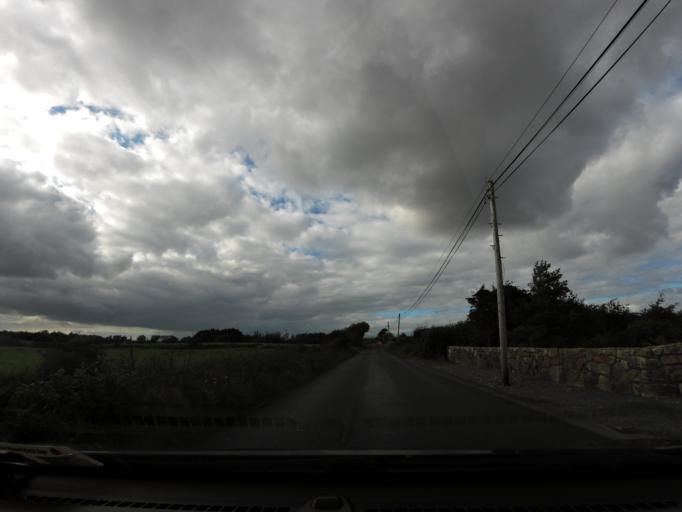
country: IE
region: Connaught
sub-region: County Galway
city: Bearna
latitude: 53.2657
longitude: -9.1555
